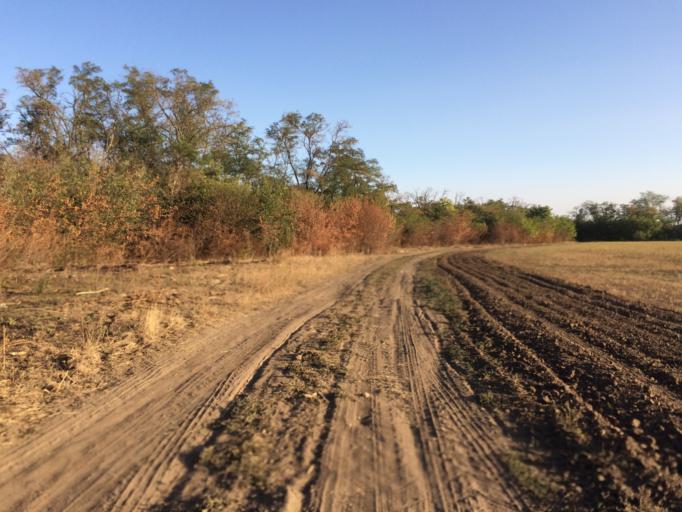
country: RU
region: Rostov
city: Gigant
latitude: 46.5120
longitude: 41.1896
